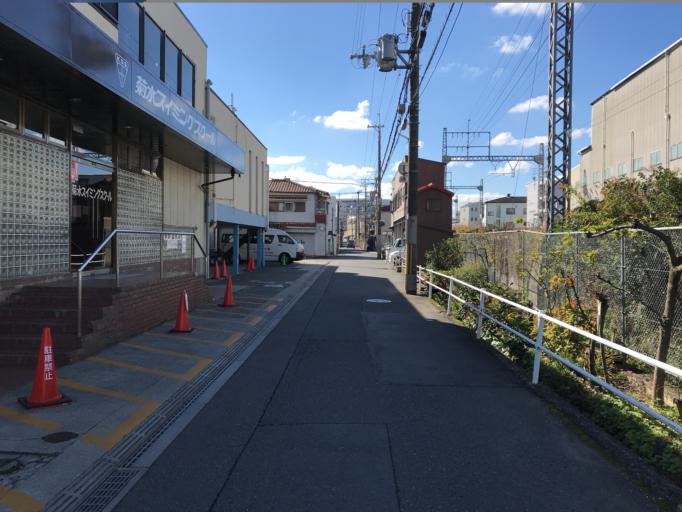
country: JP
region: Osaka
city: Tondabayashicho
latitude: 34.4546
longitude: 135.5760
